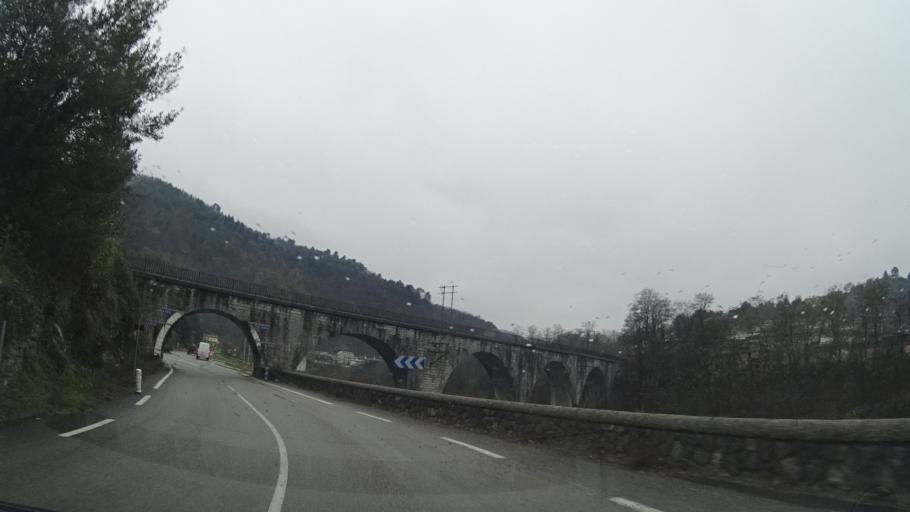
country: FR
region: Rhone-Alpes
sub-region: Departement de l'Ardeche
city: Labegude
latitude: 44.6480
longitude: 4.3555
